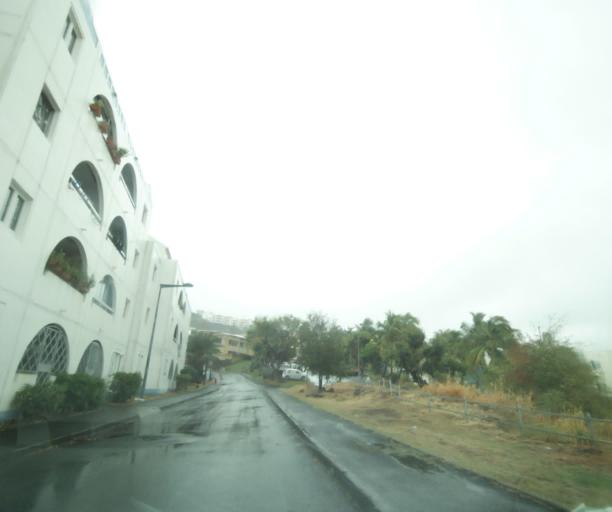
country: RE
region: Reunion
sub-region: Reunion
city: Saint-Paul
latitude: -21.0240
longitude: 55.2651
